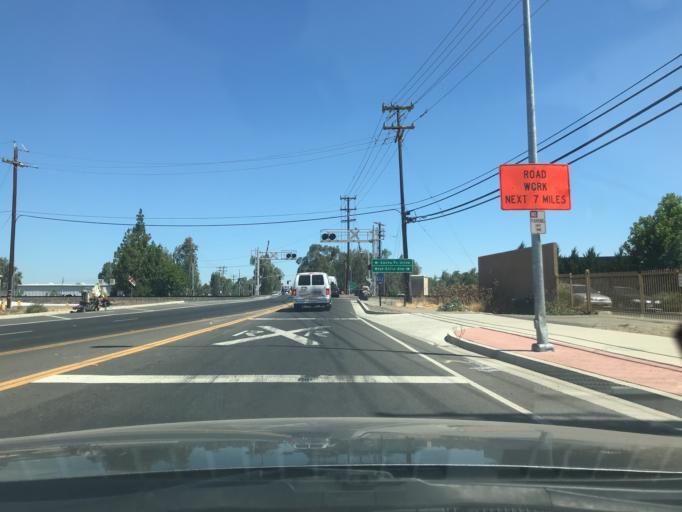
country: US
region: California
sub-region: Merced County
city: Merced
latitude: 37.3175
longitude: -120.5050
